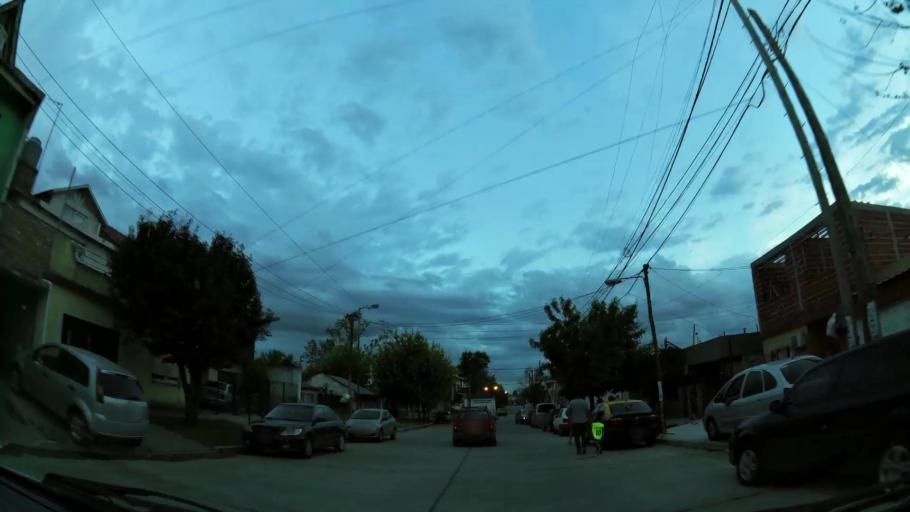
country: AR
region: Buenos Aires
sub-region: Partido de Quilmes
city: Quilmes
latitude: -34.7464
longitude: -58.2473
